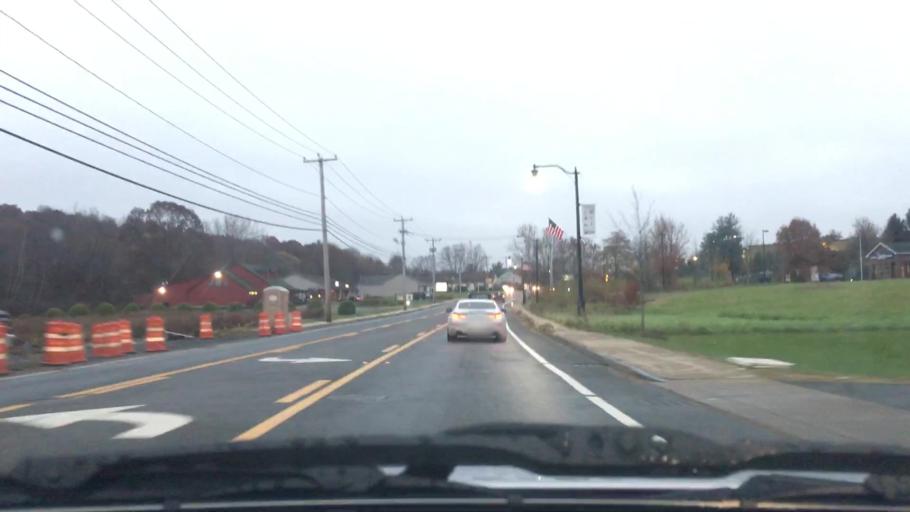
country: US
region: Massachusetts
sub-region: Hampden County
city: Southwick
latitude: 42.0686
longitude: -72.7642
